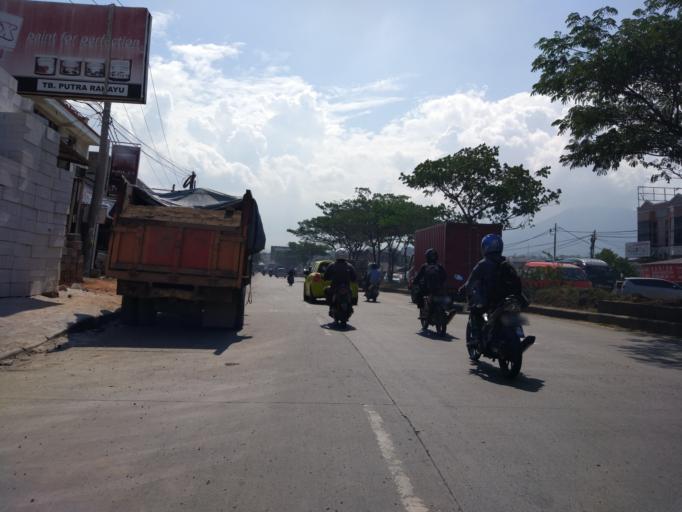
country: ID
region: West Java
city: Cileunyi
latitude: -6.9447
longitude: 107.7576
